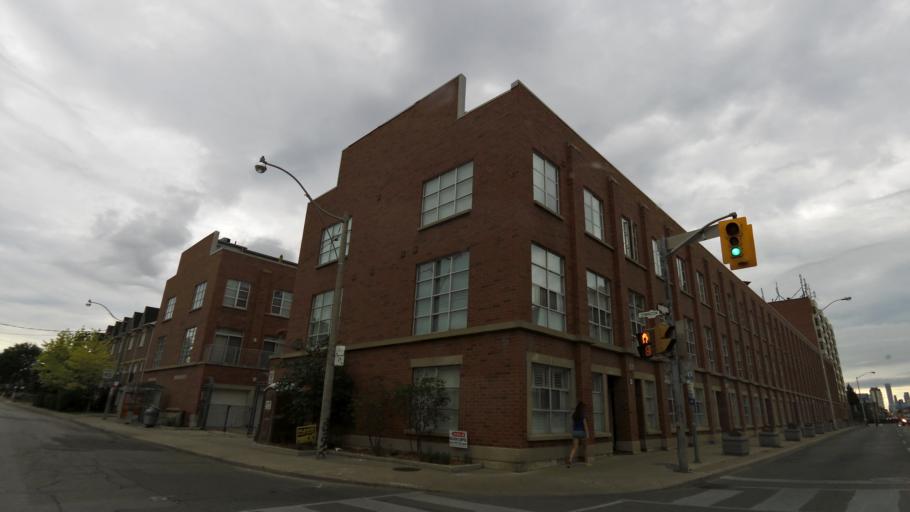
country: CA
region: Ontario
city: Toronto
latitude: 43.6573
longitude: -79.4478
